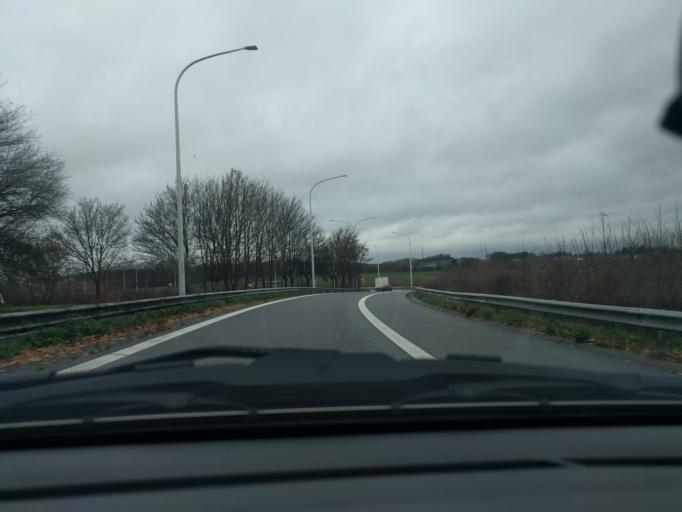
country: BE
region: Wallonia
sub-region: Province de Namur
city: Floreffe
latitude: 50.4953
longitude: 4.7905
